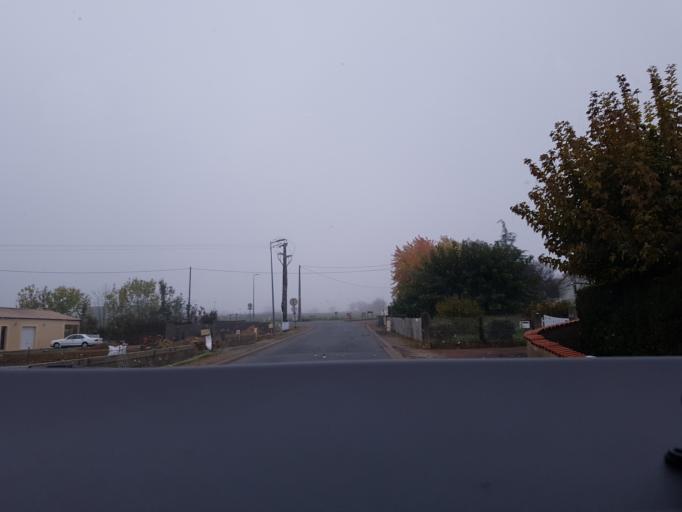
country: FR
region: Poitou-Charentes
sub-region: Departement des Deux-Sevres
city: Exireuil
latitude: 46.4282
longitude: -0.2018
